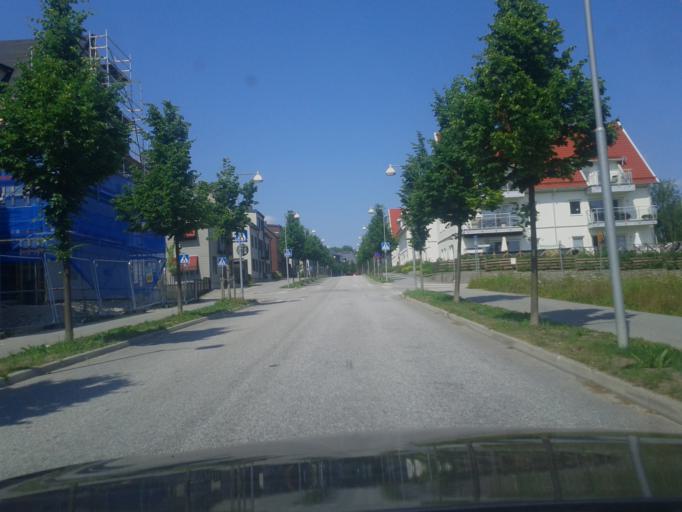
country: SE
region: Stockholm
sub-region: Vallentuna Kommun
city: Vallentuna
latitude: 59.4984
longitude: 18.0906
